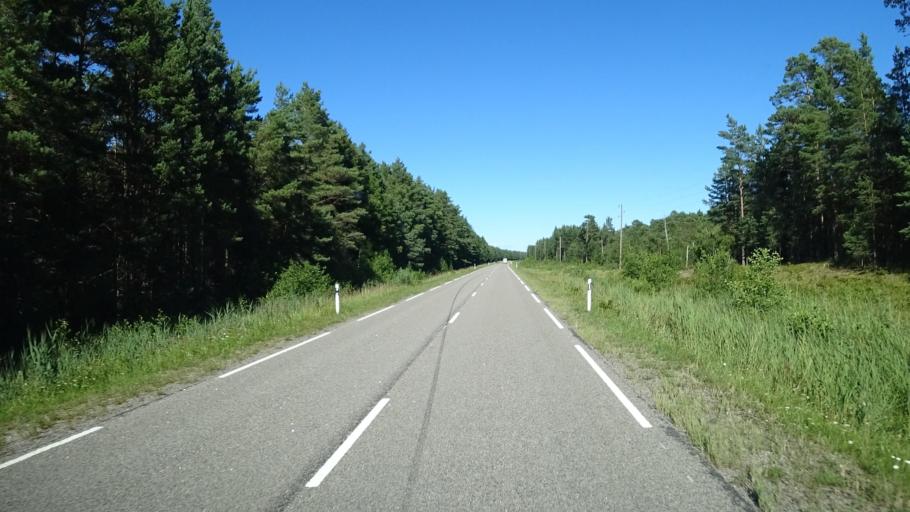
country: LV
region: Dundaga
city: Dundaga
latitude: 57.7126
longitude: 22.4532
